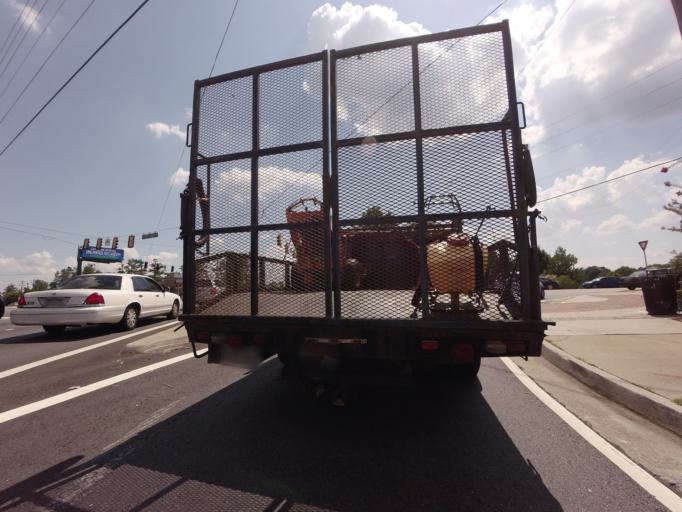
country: US
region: Georgia
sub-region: Fulton County
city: Johns Creek
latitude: 34.0470
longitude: -84.2229
